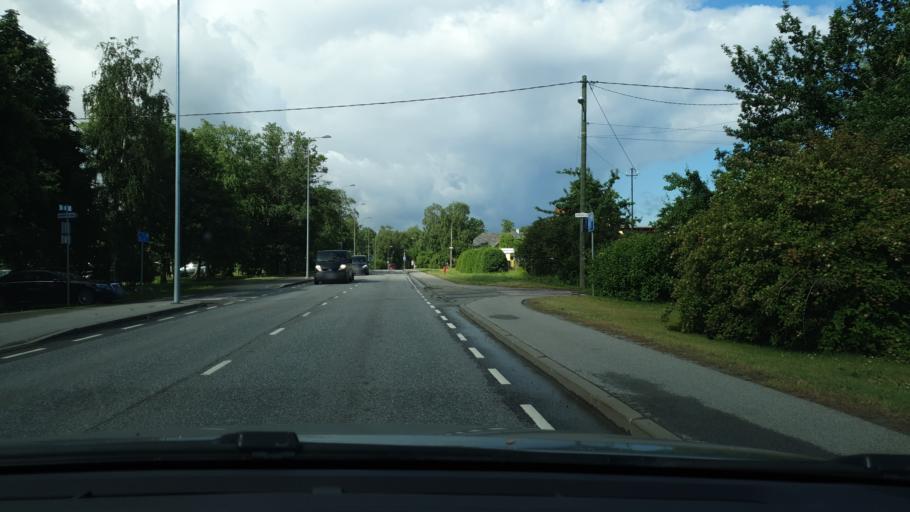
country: EE
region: Harju
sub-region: Viimsi vald
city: Viimsi
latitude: 59.4881
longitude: 24.8701
